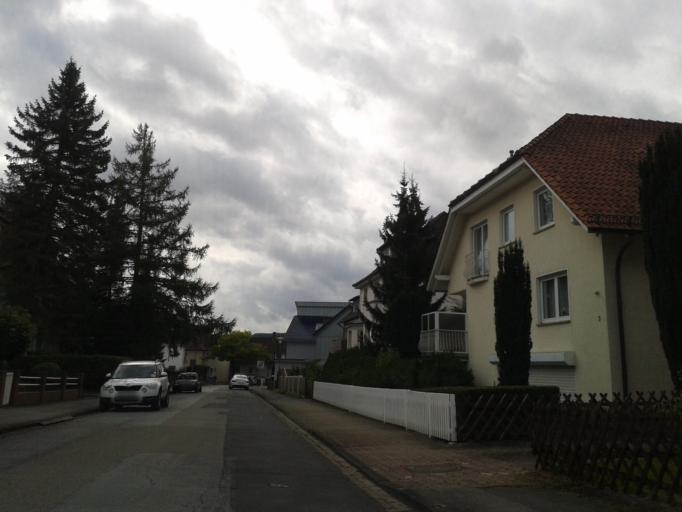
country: DE
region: Lower Saxony
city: Bad Pyrmont
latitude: 51.9851
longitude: 9.2433
